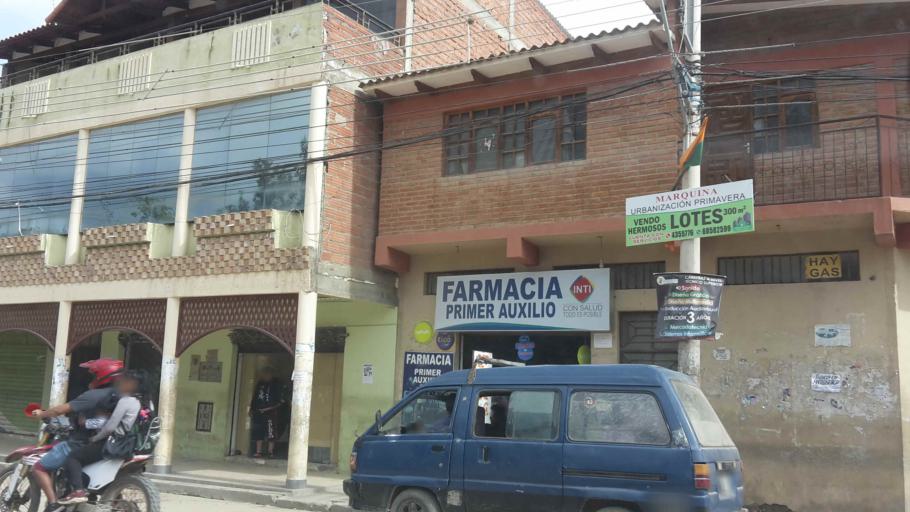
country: BO
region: Cochabamba
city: Cochabamba
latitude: -17.3385
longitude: -66.2660
